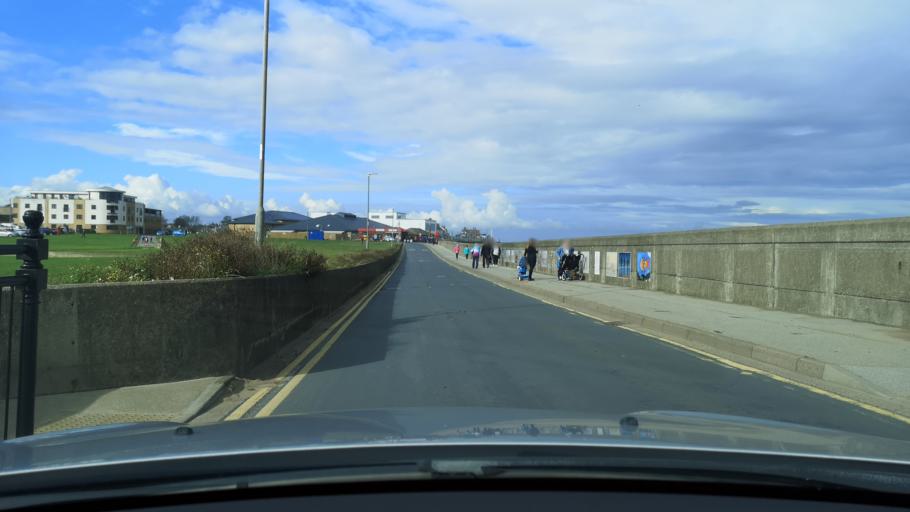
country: GB
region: England
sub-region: East Riding of Yorkshire
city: Hornsea
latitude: 53.9103
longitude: -0.1593
